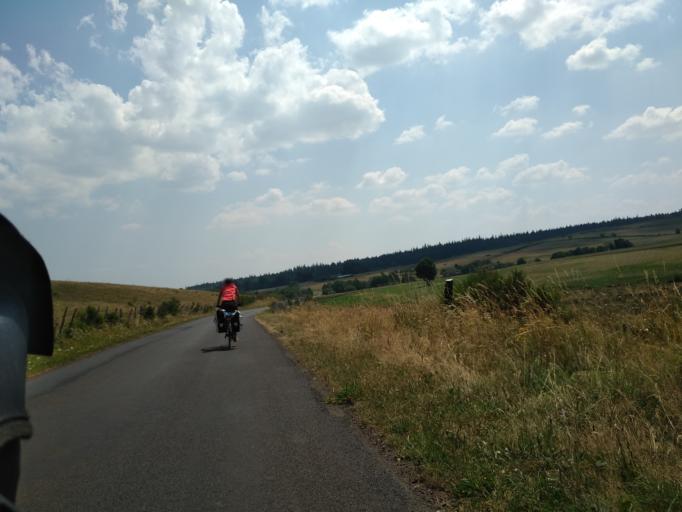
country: FR
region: Auvergne
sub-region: Departement du Puy-de-Dome
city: Mont-Dore
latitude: 45.5481
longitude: 2.8910
